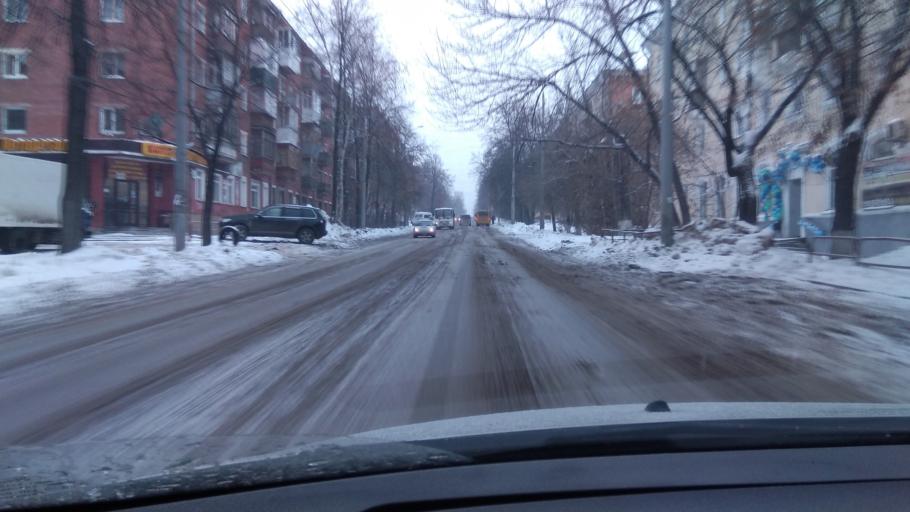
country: RU
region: Sverdlovsk
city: Yekaterinburg
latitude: 56.8931
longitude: 60.5849
